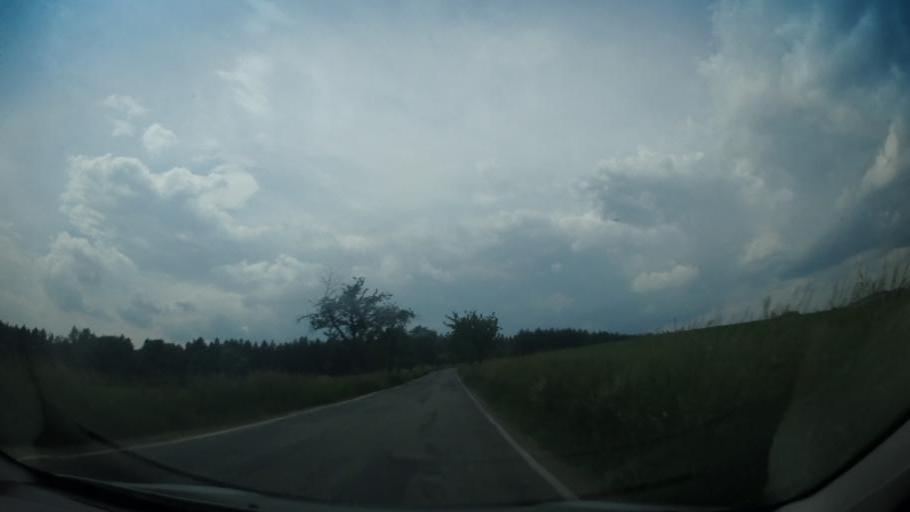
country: CZ
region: South Moravian
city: Lysice
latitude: 49.4546
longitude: 16.5000
